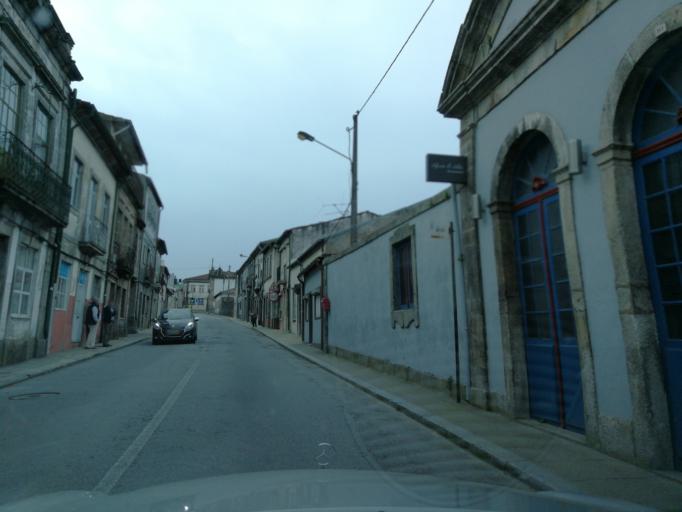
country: PT
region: Braga
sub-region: Braga
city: Braga
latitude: 41.5584
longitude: -8.4450
